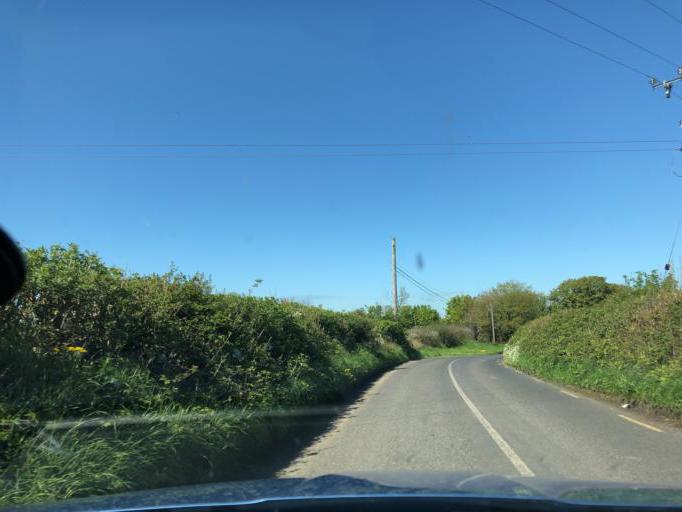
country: IE
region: Connaught
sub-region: County Galway
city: Portumna
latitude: 53.1599
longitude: -8.2509
